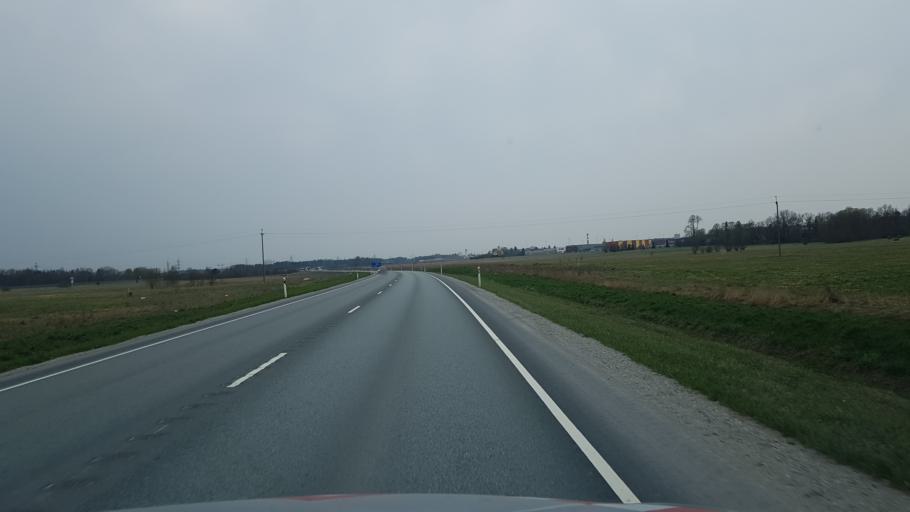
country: EE
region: Harju
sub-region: Saue vald
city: Laagri
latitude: 59.3289
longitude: 24.6323
